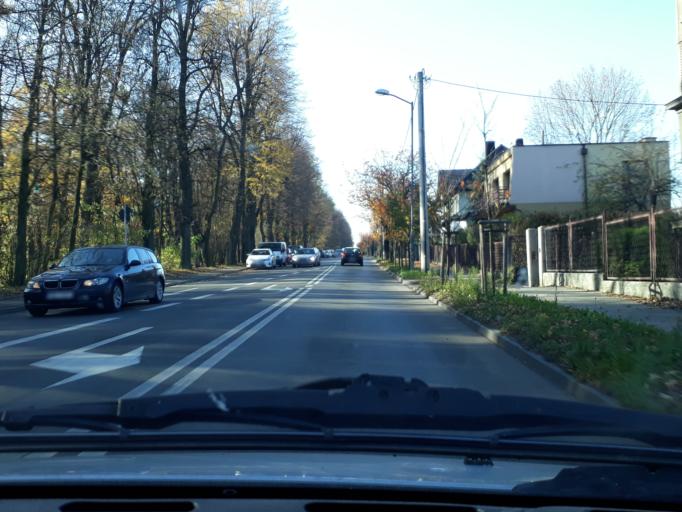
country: PL
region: Silesian Voivodeship
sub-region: Powiat tarnogorski
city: Tarnowskie Gory
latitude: 50.4423
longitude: 18.8467
